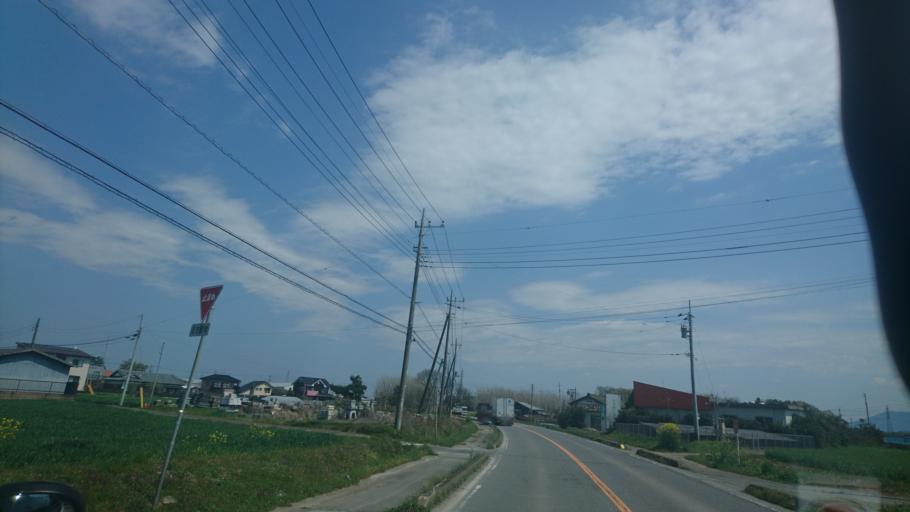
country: JP
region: Ibaraki
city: Yuki
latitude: 36.2183
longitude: 139.9209
